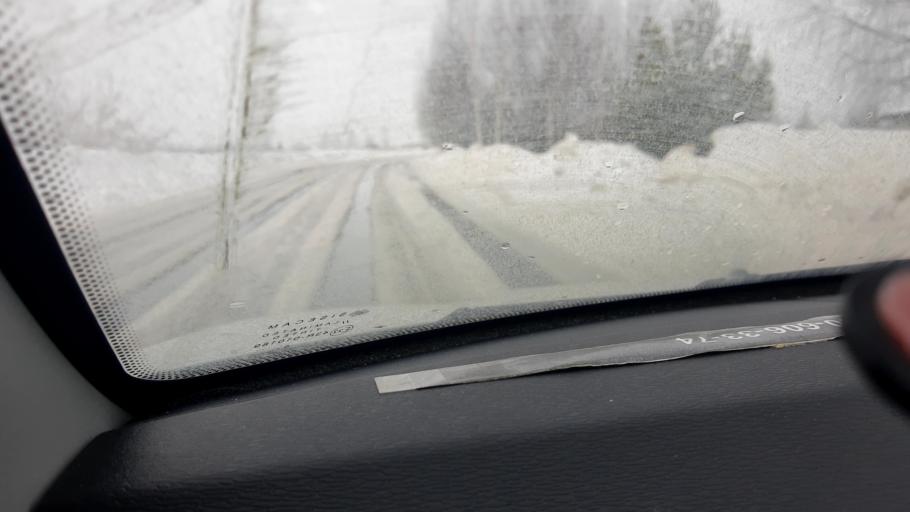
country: RU
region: Nizjnij Novgorod
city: Sitniki
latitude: 56.5228
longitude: 44.0411
